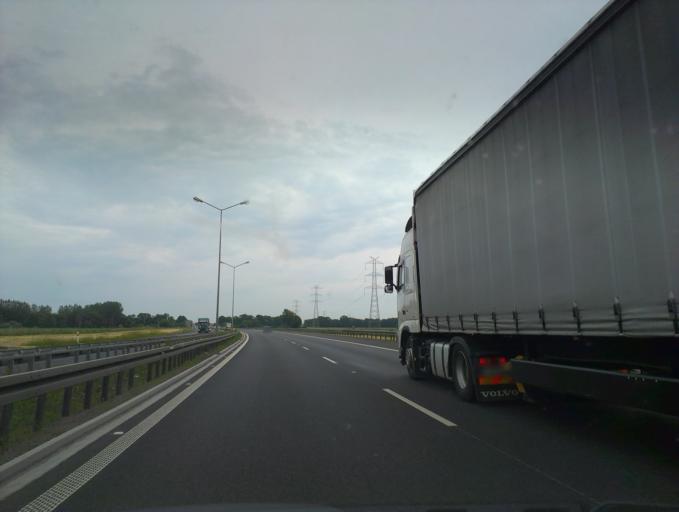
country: PL
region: Lower Silesian Voivodeship
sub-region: Powiat strzelinski
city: Wiazow
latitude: 50.8409
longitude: 17.2632
